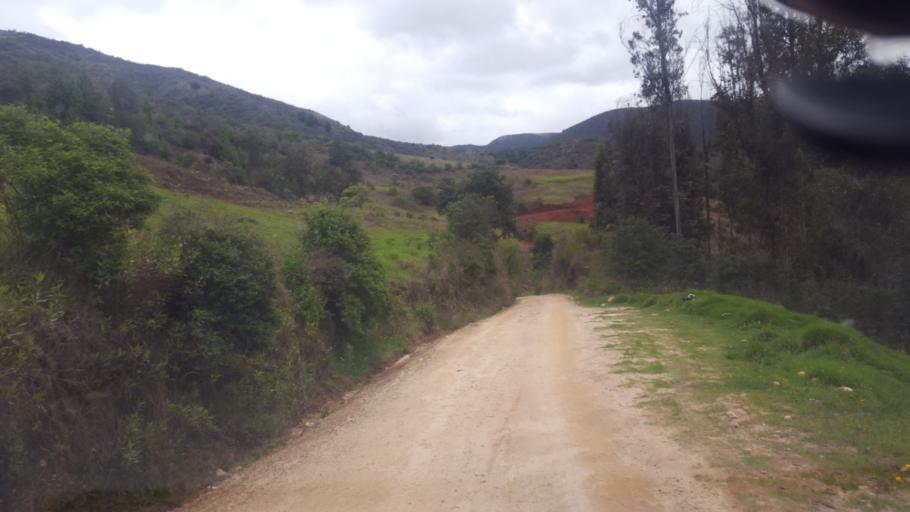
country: CO
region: Boyaca
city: Belen
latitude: 6.0148
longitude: -72.8745
